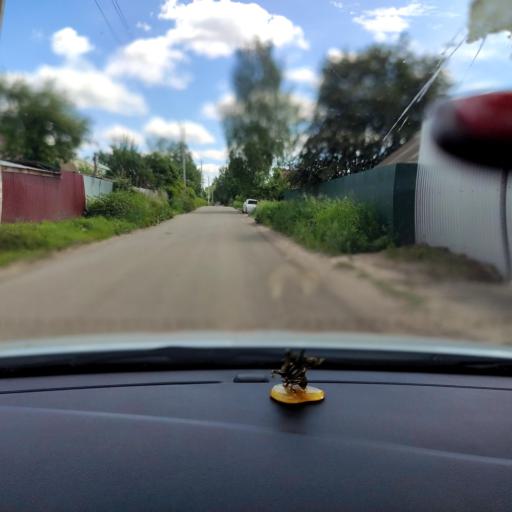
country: RU
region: Tatarstan
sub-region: Zelenodol'skiy Rayon
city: Vasil'yevo
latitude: 55.8288
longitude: 48.7454
